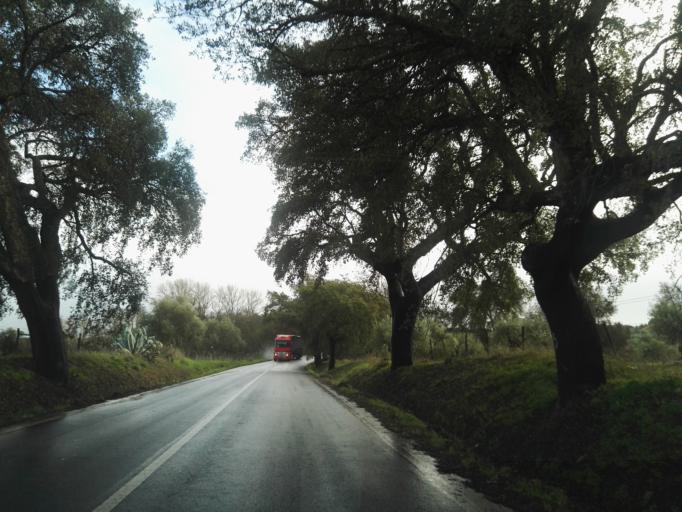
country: PT
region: Portalegre
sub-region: Elvas
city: Elvas
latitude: 38.9430
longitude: -7.1977
